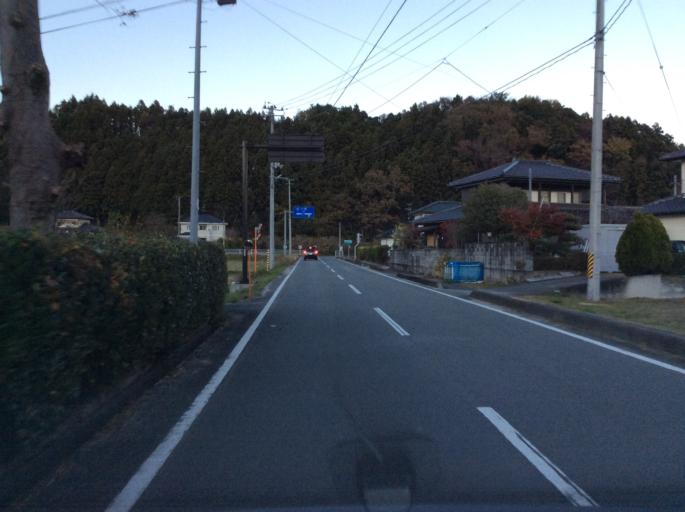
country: JP
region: Fukushima
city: Iwaki
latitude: 37.1357
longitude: 140.8517
